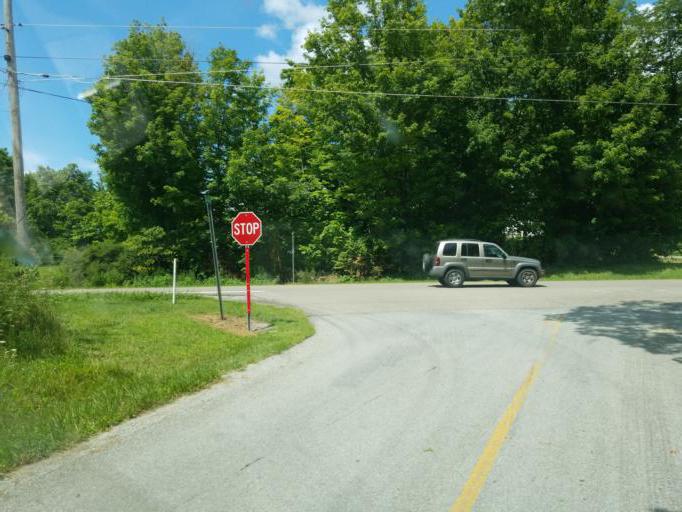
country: US
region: Ohio
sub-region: Delaware County
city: Sunbury
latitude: 40.3187
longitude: -82.8302
